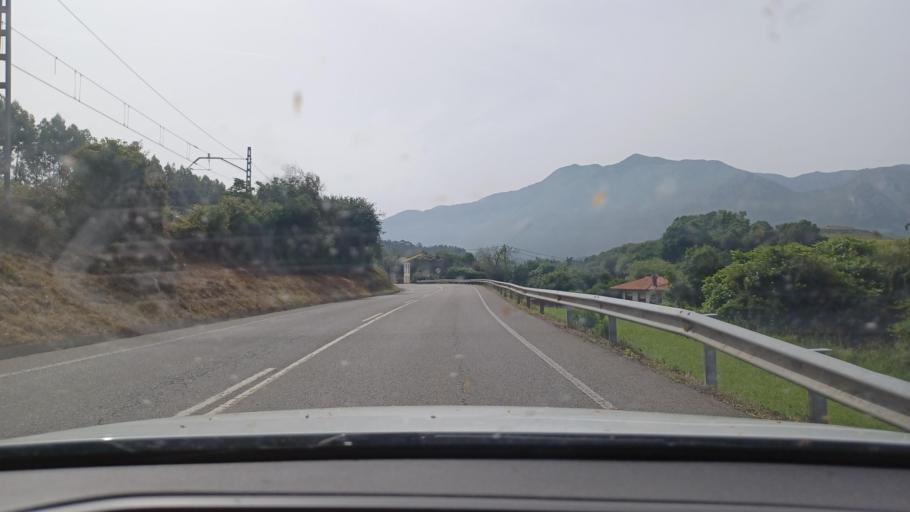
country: ES
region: Asturias
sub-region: Province of Asturias
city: Ribadesella
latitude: 43.4590
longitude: -5.0458
